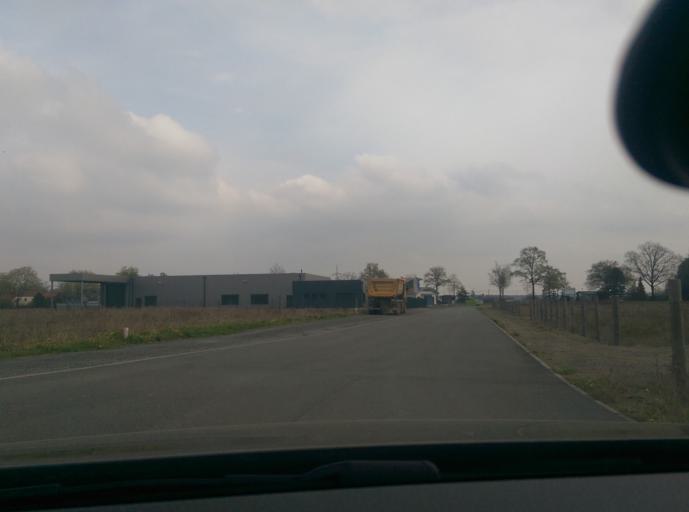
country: DE
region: Lower Saxony
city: Elze
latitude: 52.5869
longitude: 9.7258
